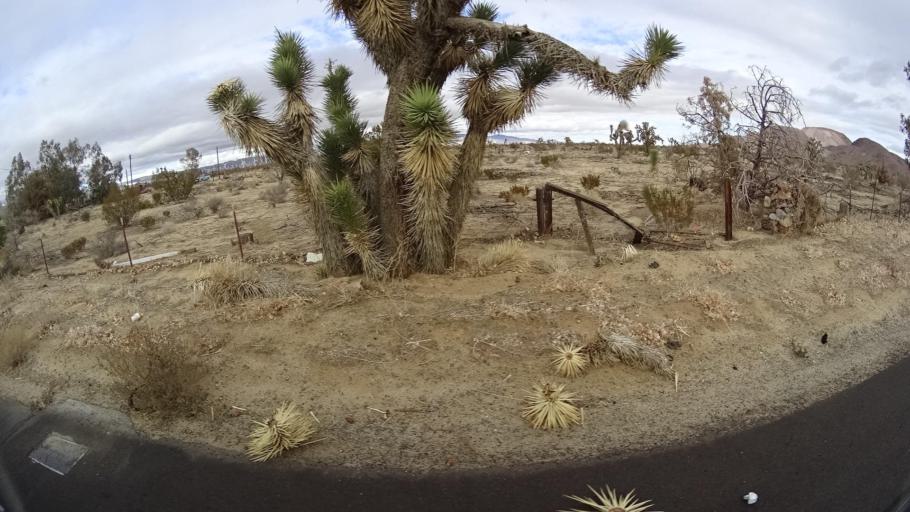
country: US
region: California
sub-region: Kern County
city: Rosamond
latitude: 34.9509
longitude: -118.2293
